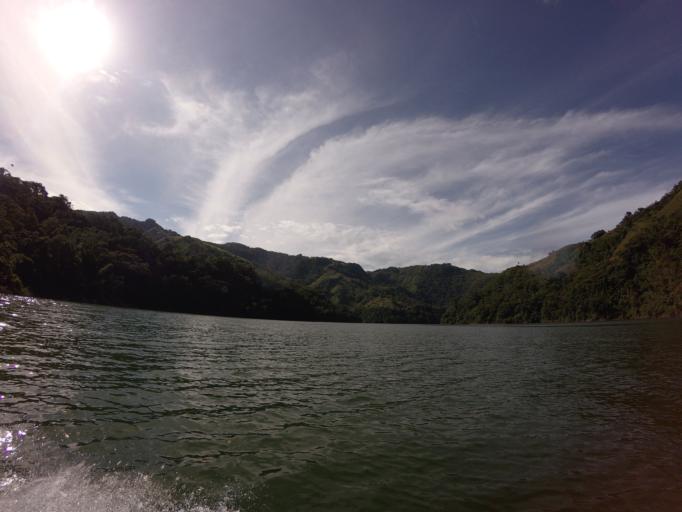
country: CO
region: Caldas
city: Norcasia
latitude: 5.5265
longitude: -74.9316
